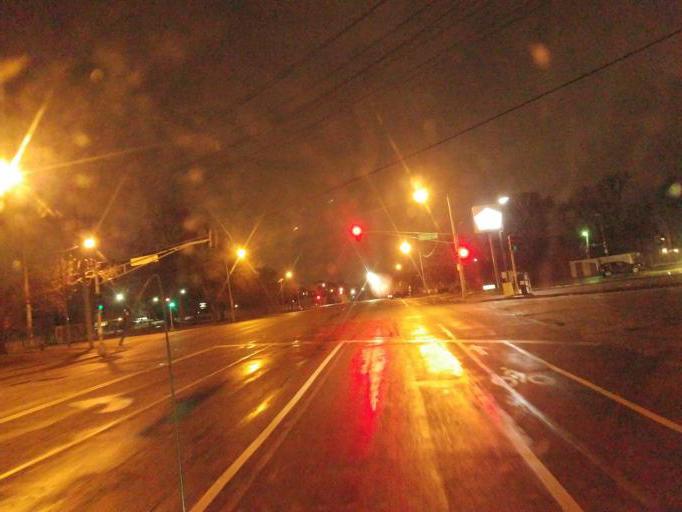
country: US
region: Missouri
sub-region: City of Saint Louis
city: St. Louis
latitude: 38.6547
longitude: -90.2022
